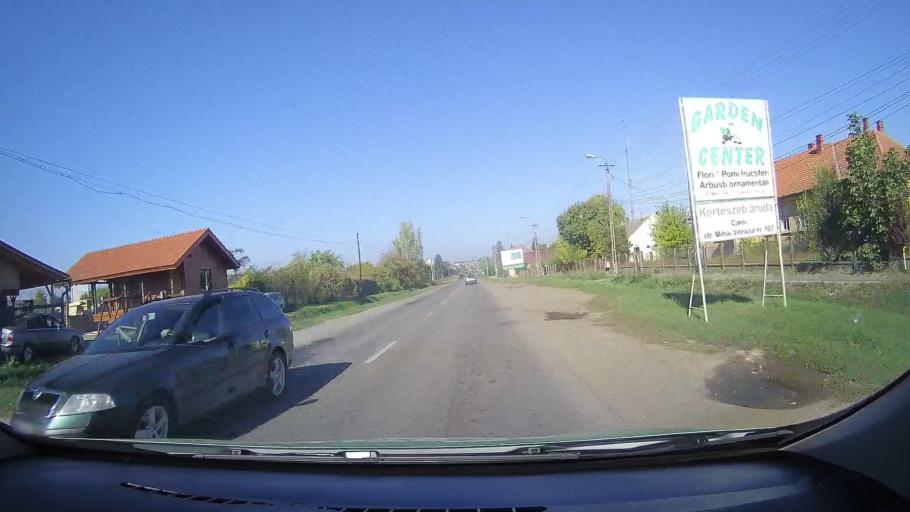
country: RO
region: Satu Mare
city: Carei
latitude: 47.6753
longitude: 22.4794
